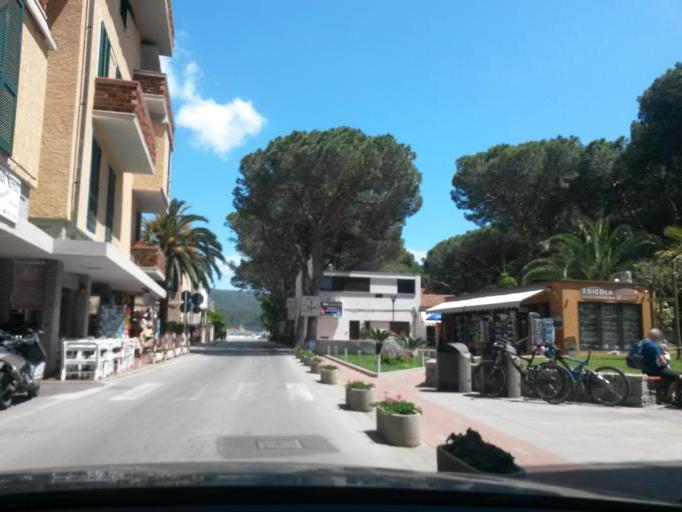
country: IT
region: Tuscany
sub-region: Provincia di Livorno
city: Campo nell'Elba
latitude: 42.7459
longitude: 10.2335
